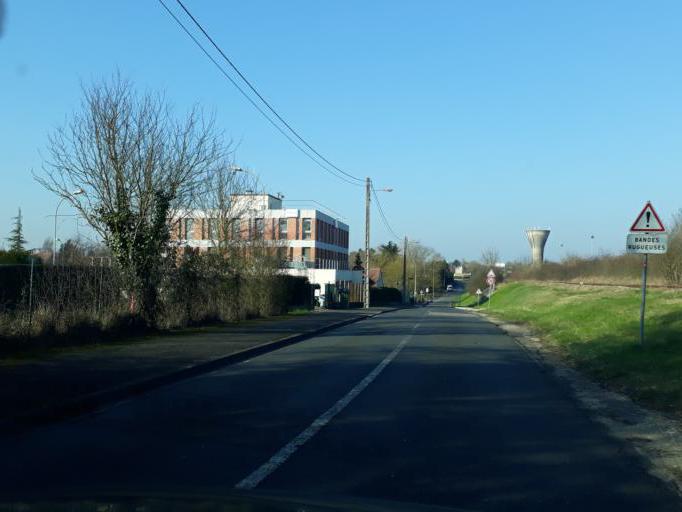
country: FR
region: Centre
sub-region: Departement du Loiret
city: Semoy
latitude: 47.9085
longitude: 1.9455
